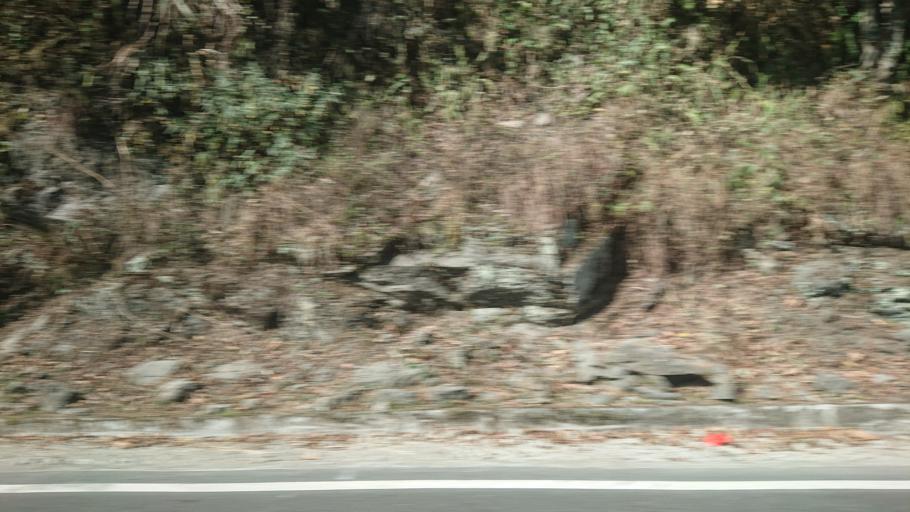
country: TW
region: Taiwan
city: Lugu
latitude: 23.4703
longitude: 120.7302
